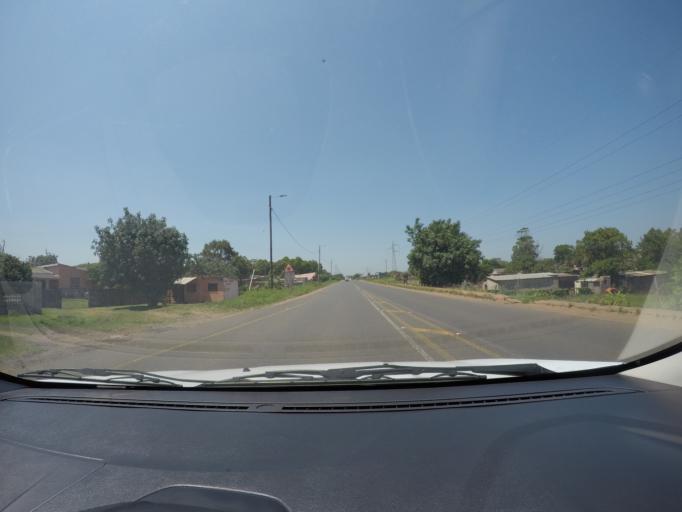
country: ZA
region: KwaZulu-Natal
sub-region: uThungulu District Municipality
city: eSikhawini
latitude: -28.8400
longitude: 31.9357
